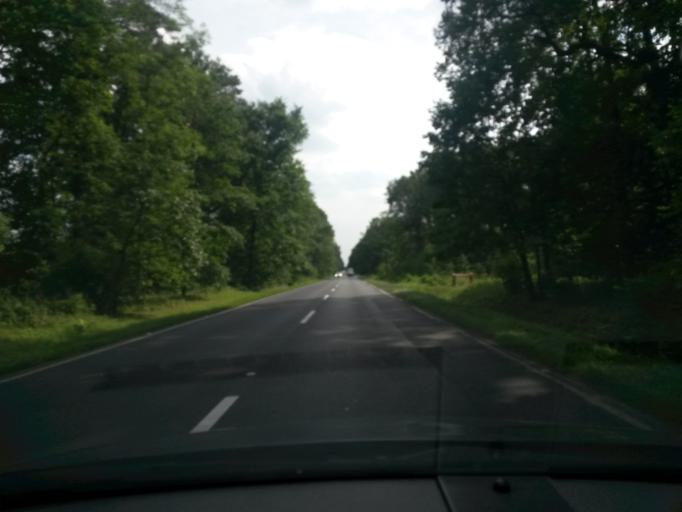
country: PL
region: Greater Poland Voivodeship
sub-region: Powiat poznanski
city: Kornik
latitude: 52.2060
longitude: 17.0670
